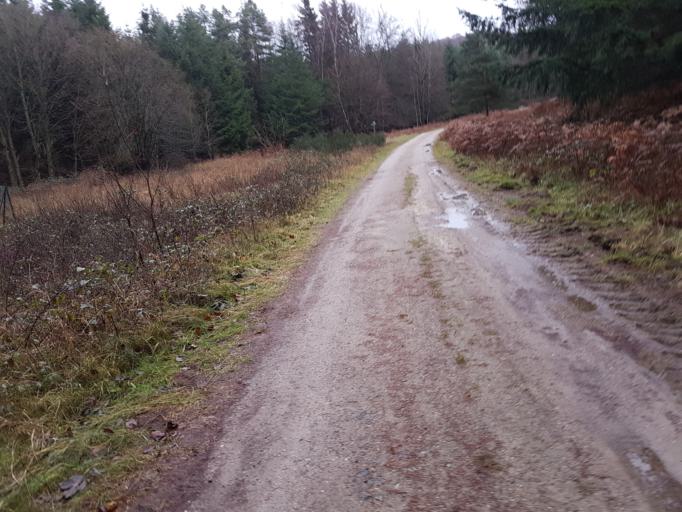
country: DE
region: Mecklenburg-Vorpommern
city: Ostseebad Binz
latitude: 54.3907
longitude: 13.6276
